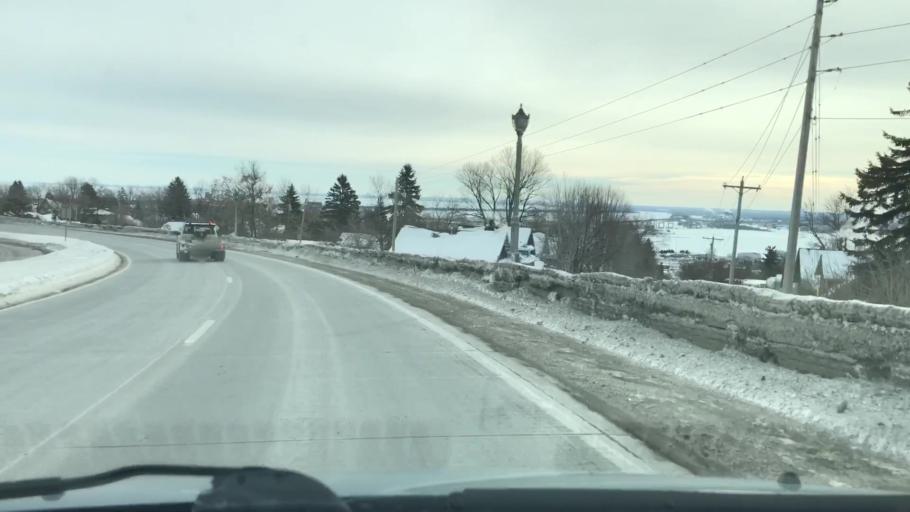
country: US
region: Minnesota
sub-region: Saint Louis County
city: Duluth
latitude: 46.7714
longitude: -92.1370
